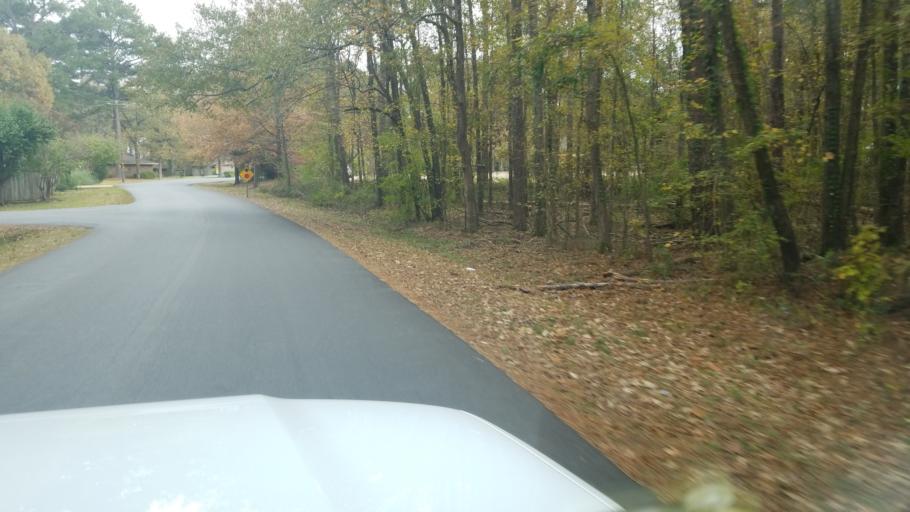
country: US
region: Mississippi
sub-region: Madison County
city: Ridgeland
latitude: 32.3818
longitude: -90.0326
